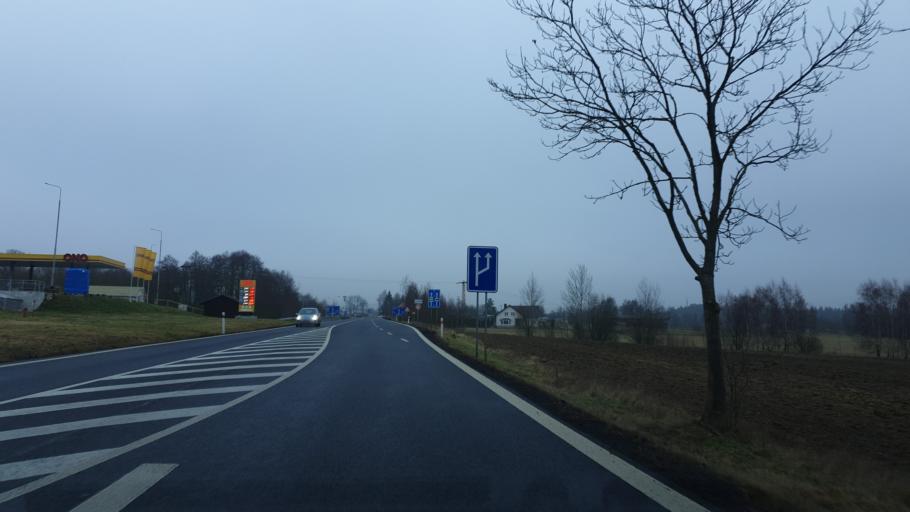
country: CZ
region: Karlovarsky
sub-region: Okres Cheb
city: Skalna
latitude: 50.1624
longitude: 12.3196
